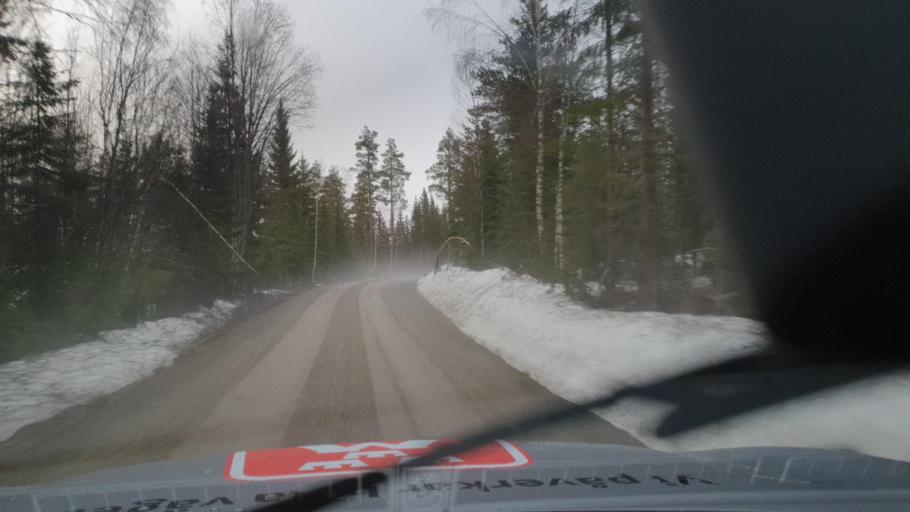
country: SE
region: Vaesternorrland
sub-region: OErnskoeldsviks Kommun
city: Bjasta
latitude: 63.2186
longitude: 18.2889
